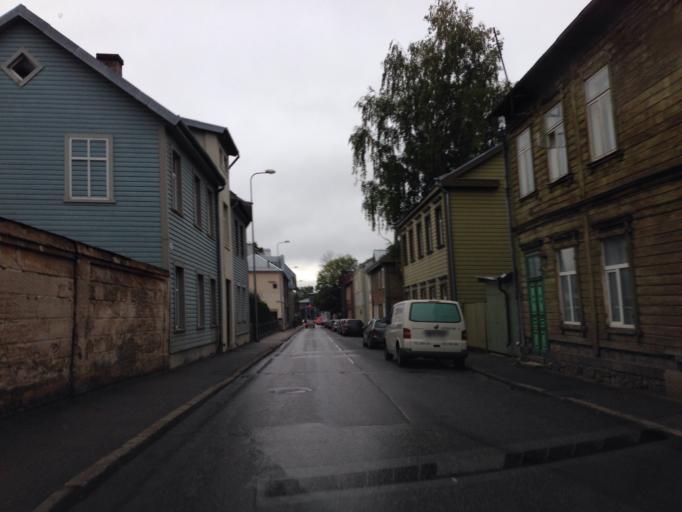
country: EE
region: Tartu
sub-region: Tartu linn
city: Tartu
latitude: 58.3728
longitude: 26.7133
